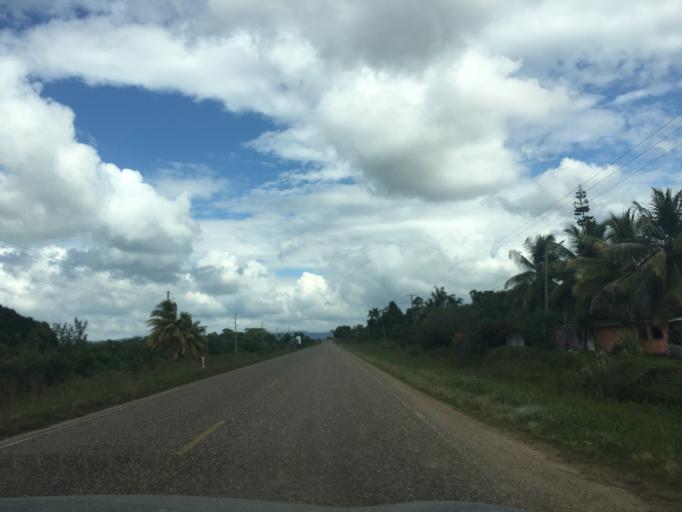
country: BZ
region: Stann Creek
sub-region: Dangriga
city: Dangriga
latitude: 16.8565
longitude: -88.3463
